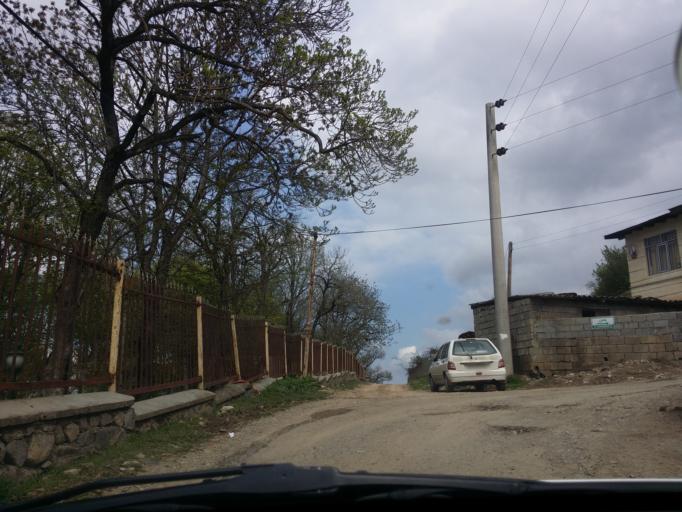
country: IR
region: Mazandaran
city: `Abbasabad
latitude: 36.4898
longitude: 51.1521
